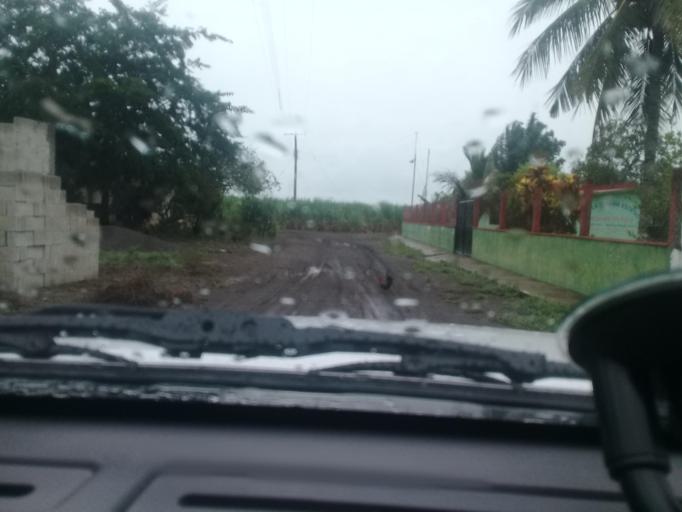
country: MX
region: Veracruz
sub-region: Puente Nacional
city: Cabezas
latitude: 19.3573
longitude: -96.3776
